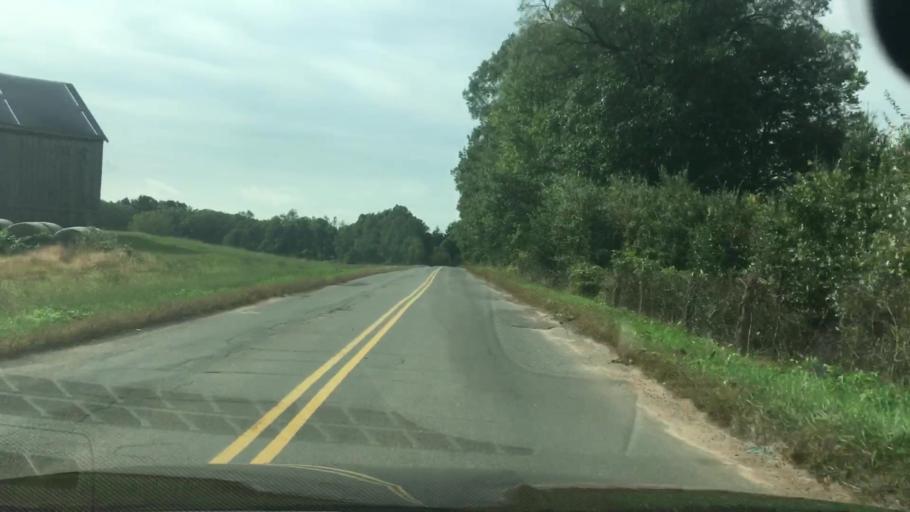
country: US
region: Connecticut
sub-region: Hartford County
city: Broad Brook
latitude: 41.8779
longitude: -72.5492
